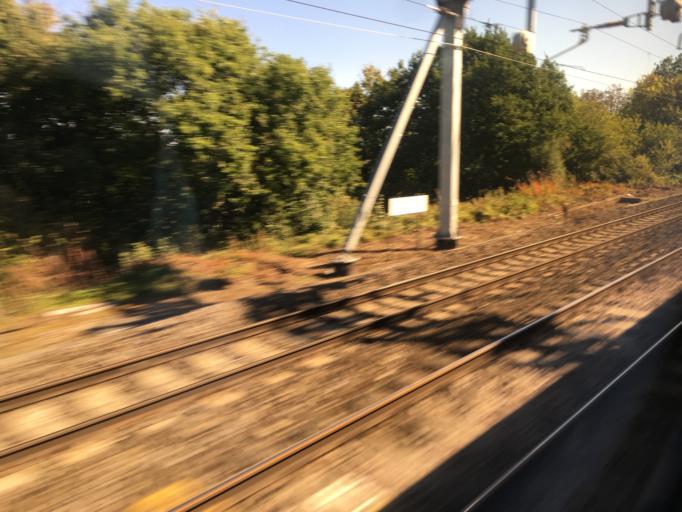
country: GB
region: England
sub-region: West Berkshire
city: Tilehurst
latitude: 51.4701
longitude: -1.0265
